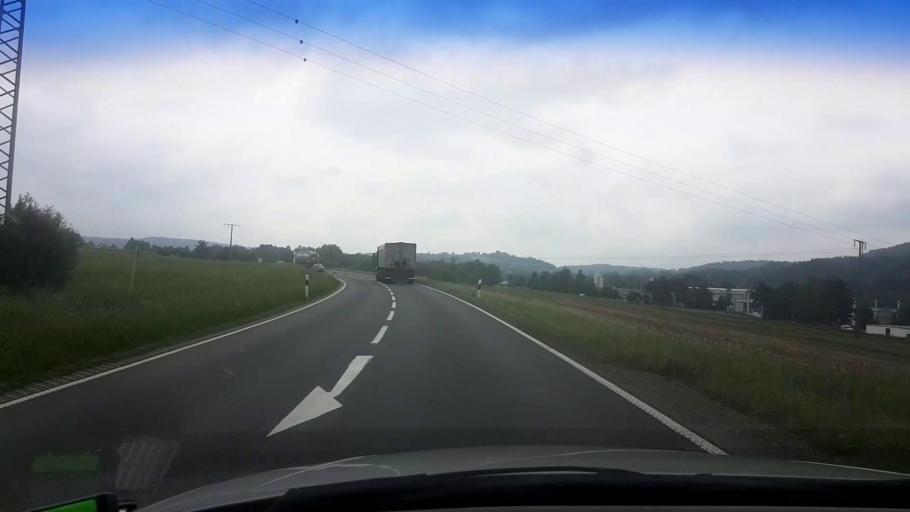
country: DE
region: Bavaria
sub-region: Upper Franconia
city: Reuth
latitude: 49.9536
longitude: 11.7057
